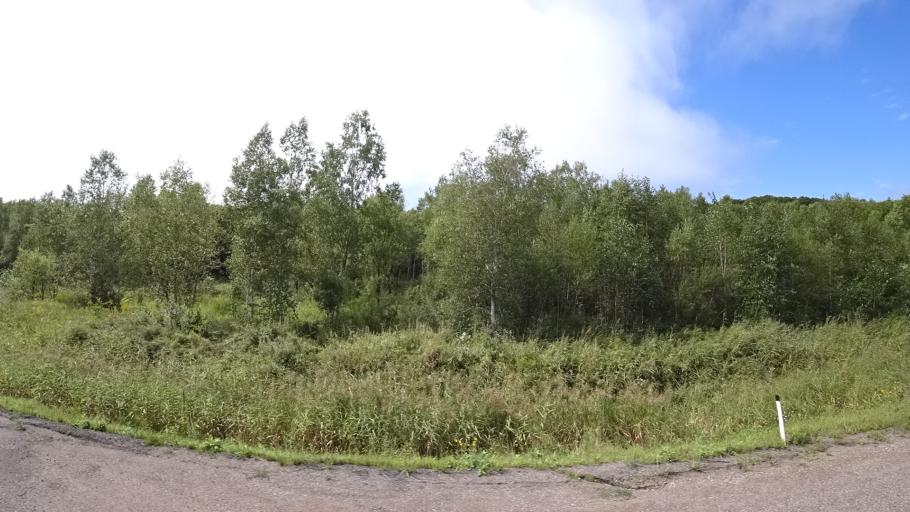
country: RU
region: Primorskiy
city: Lyalichi
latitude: 44.1176
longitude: 132.4192
